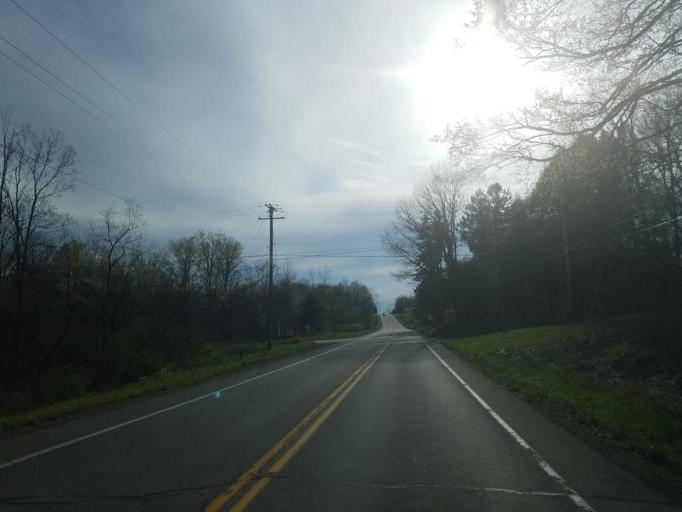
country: US
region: Pennsylvania
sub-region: Mercer County
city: Stoneboro
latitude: 41.2690
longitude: -80.1531
